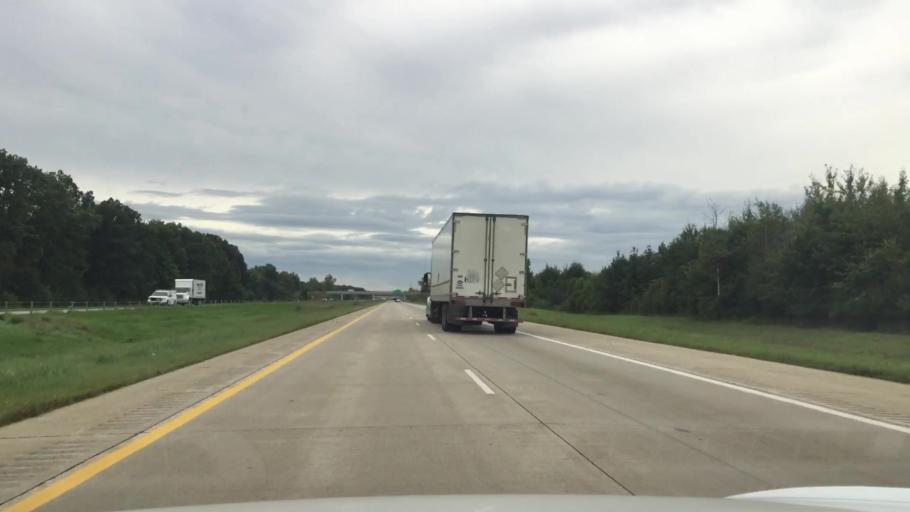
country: US
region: Michigan
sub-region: Saint Clair County
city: Marysville
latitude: 42.9409
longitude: -82.5081
